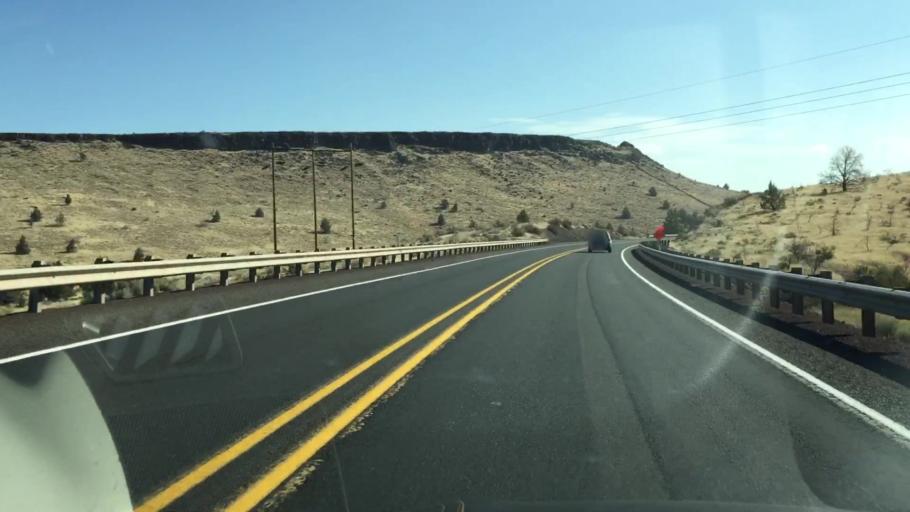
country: US
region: Oregon
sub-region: Jefferson County
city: Madras
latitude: 44.7652
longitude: -121.0132
